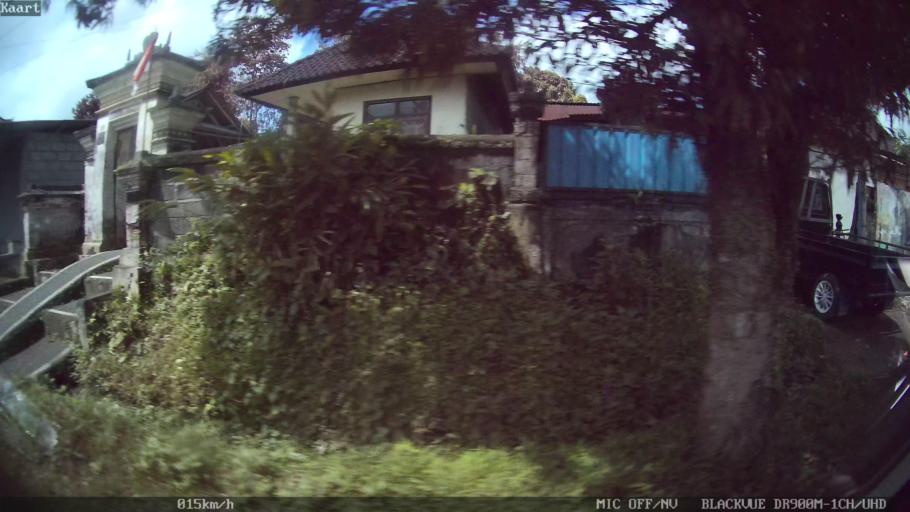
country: ID
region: Bali
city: Banjar Petak
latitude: -8.4582
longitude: 115.3205
